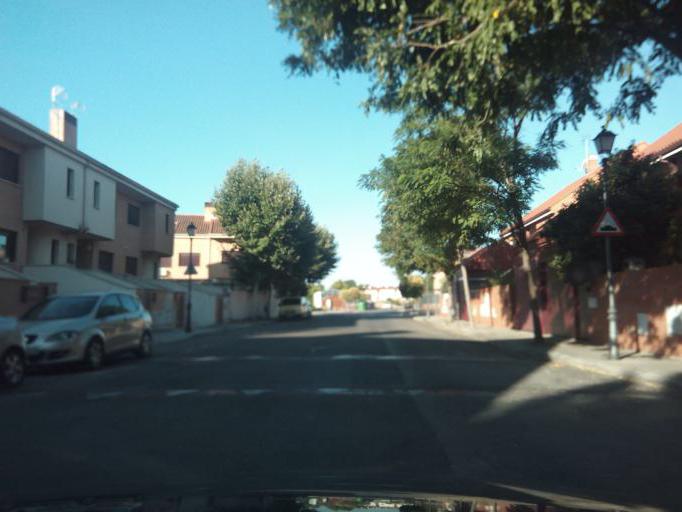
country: ES
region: Madrid
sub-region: Provincia de Madrid
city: Daganzo de Arriba
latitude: 40.5472
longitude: -3.4607
